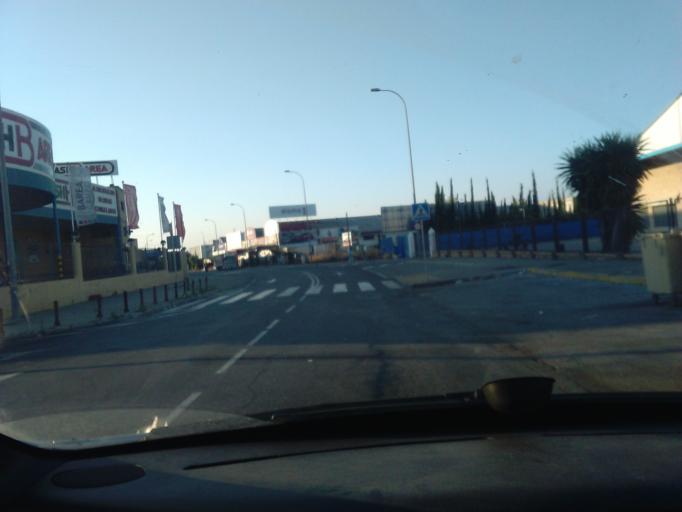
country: ES
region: Andalusia
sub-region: Provincia de Sevilla
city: Sevilla
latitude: 37.3905
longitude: -5.9454
